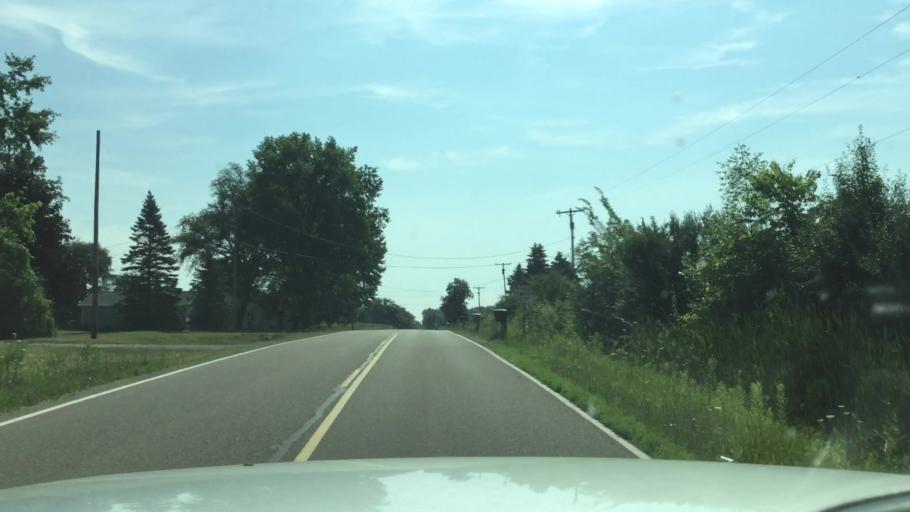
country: US
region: Michigan
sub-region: Genesee County
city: Flushing
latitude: 43.1335
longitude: -83.8252
